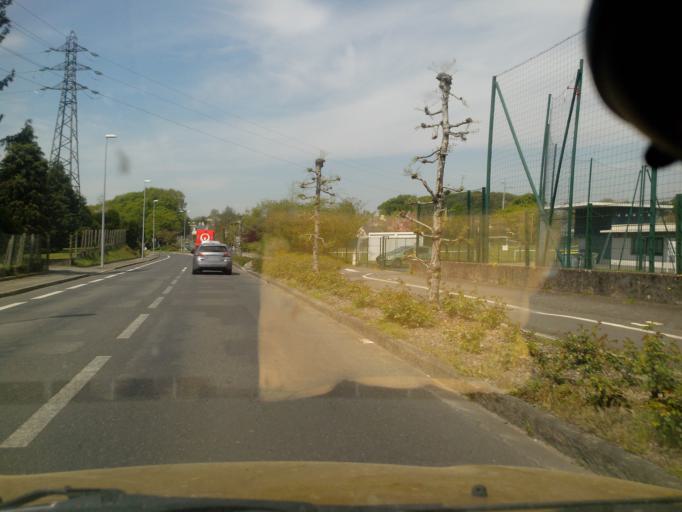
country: FR
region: Pays de la Loire
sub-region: Departement de la Loire-Atlantique
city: Orvault
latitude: 47.2533
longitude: -1.6131
